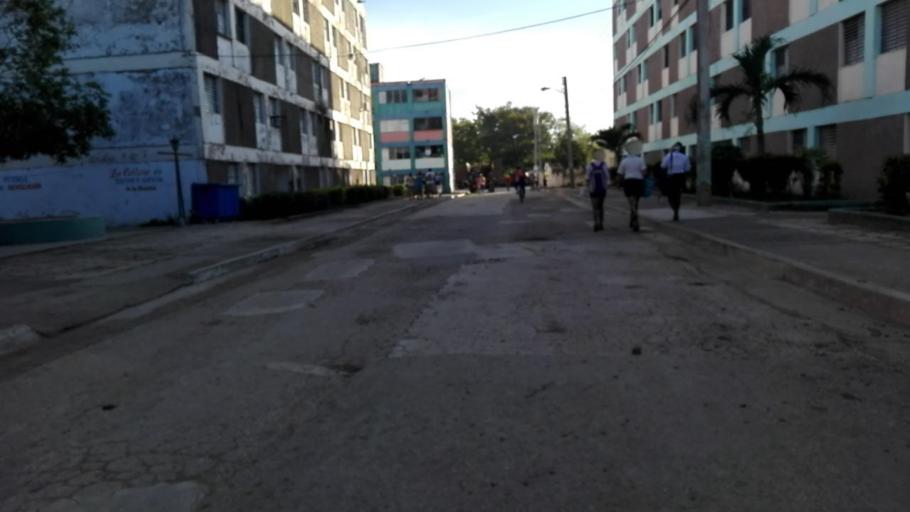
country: CU
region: Granma
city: Bartolome Maso
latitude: 20.1667
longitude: -76.9458
